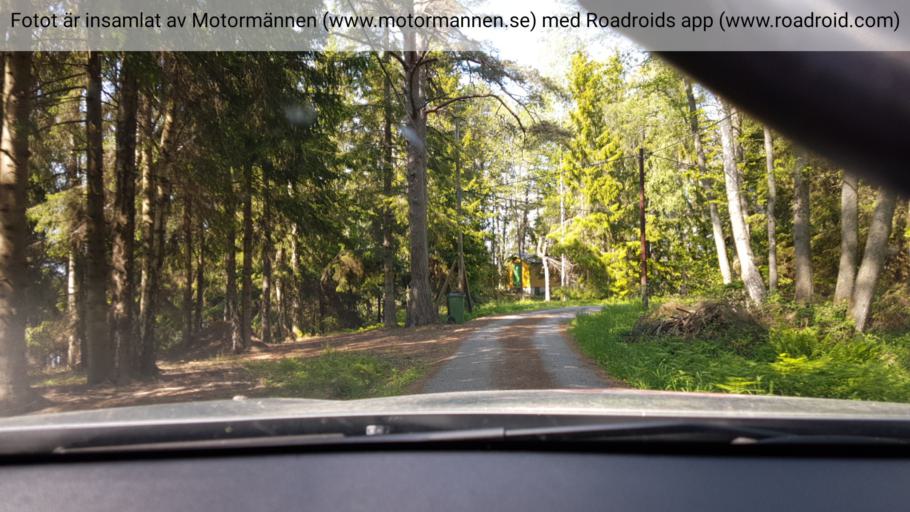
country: SE
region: Stockholm
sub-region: Haninge Kommun
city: Jordbro
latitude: 59.0149
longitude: 18.0880
